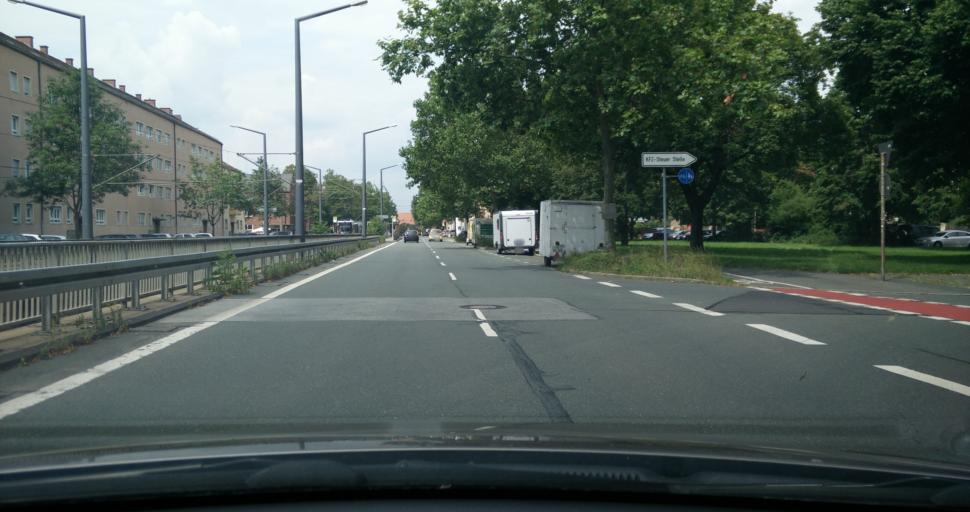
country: DE
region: Bavaria
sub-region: Regierungsbezirk Mittelfranken
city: Nuernberg
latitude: 49.4330
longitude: 11.0959
